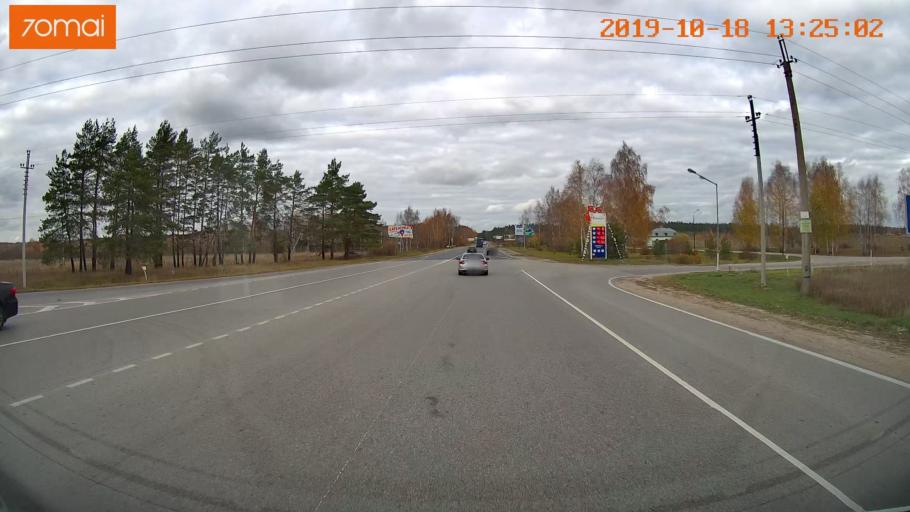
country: RU
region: Rjazan
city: Polyany
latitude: 54.7393
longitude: 39.8410
